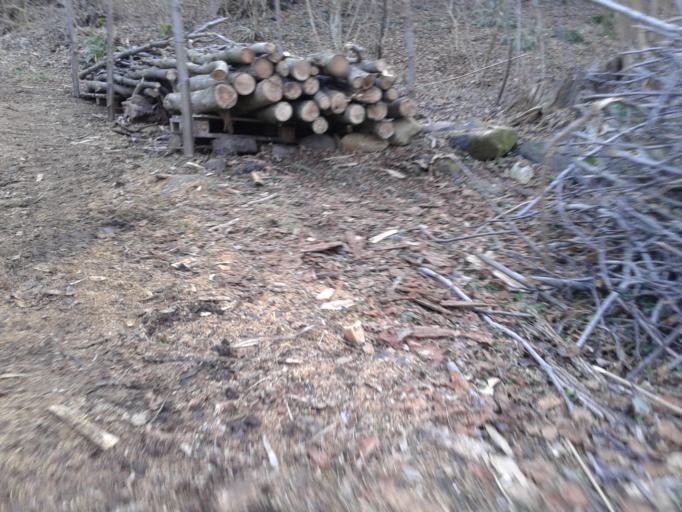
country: IT
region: Veneto
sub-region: Provincia di Vicenza
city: Monte di Malo
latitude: 45.6671
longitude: 11.3600
